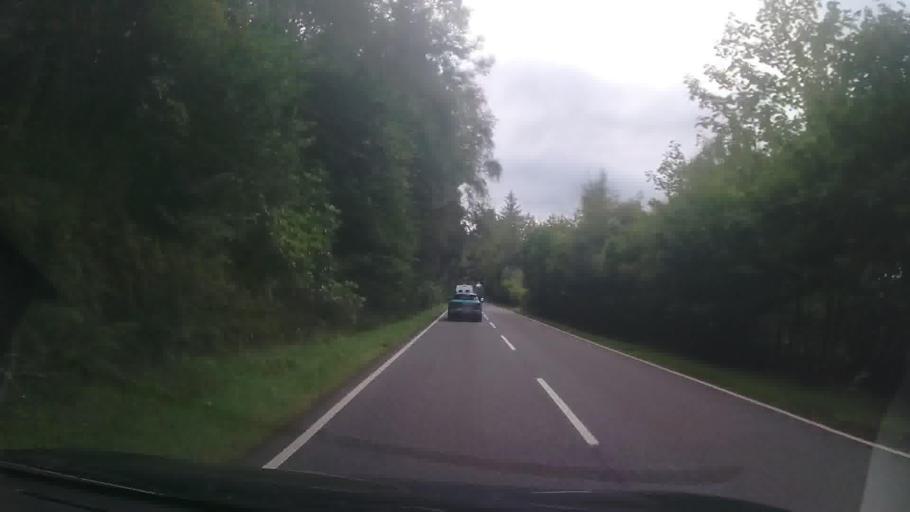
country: GB
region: Scotland
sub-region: Highland
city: Fort William
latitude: 56.6328
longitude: -5.3040
